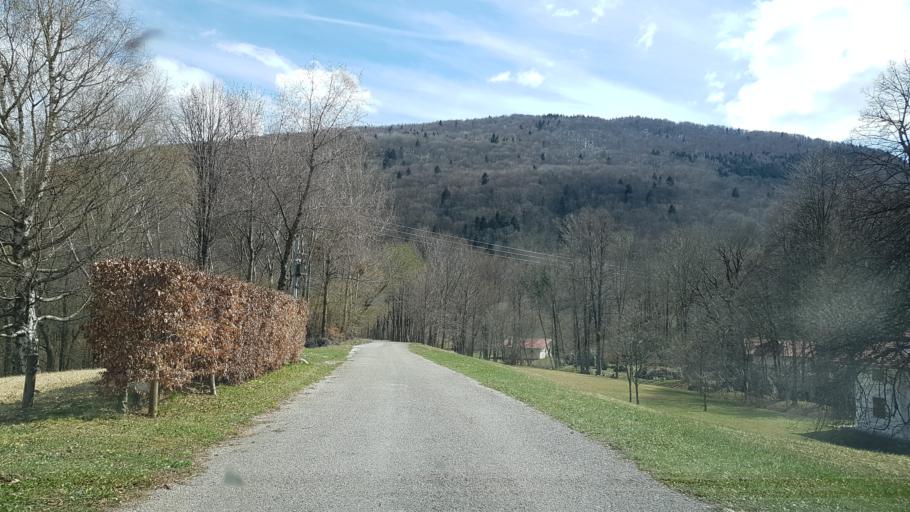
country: IT
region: Friuli Venezia Giulia
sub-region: Provincia di Udine
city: Trasaghis
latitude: 46.2863
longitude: 13.0218
